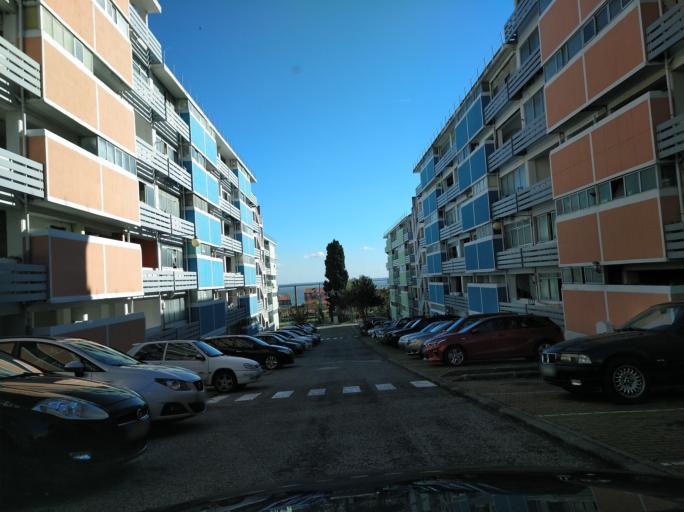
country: PT
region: Lisbon
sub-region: Loures
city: Moscavide
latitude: 38.7435
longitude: -9.1080
